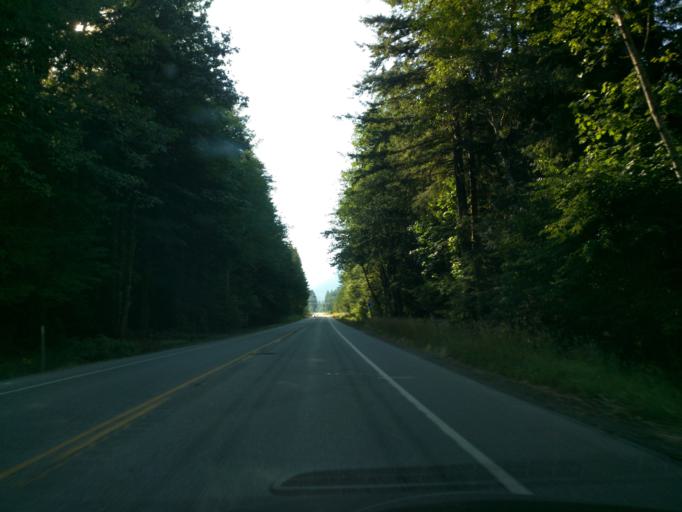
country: US
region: Washington
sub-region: Snohomish County
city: Darrington
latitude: 48.2694
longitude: -121.7280
